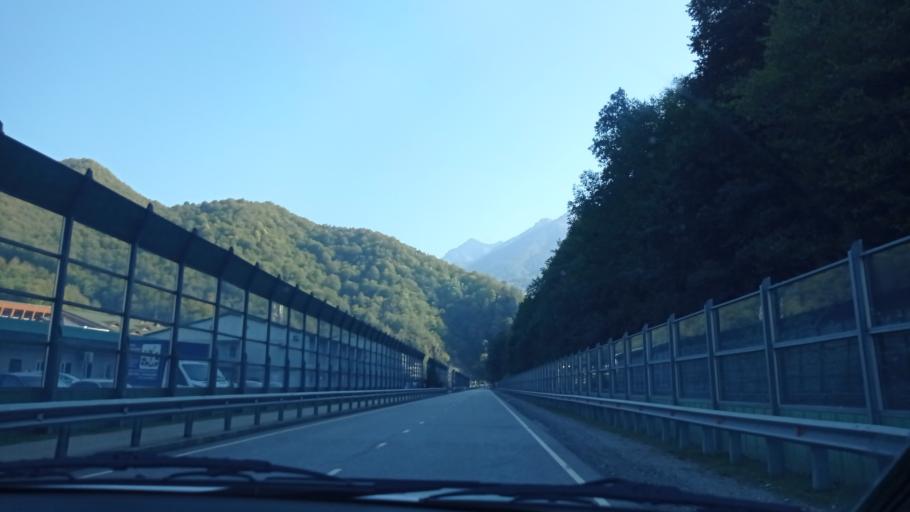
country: RU
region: Krasnodarskiy
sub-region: Sochi City
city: Krasnaya Polyana
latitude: 43.6877
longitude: 40.2751
